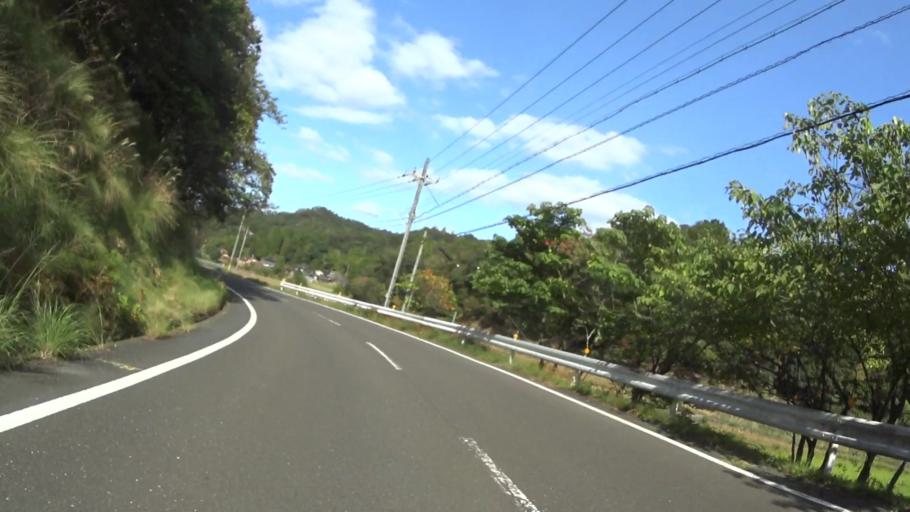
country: JP
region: Hyogo
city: Toyooka
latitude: 35.5586
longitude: 134.9796
